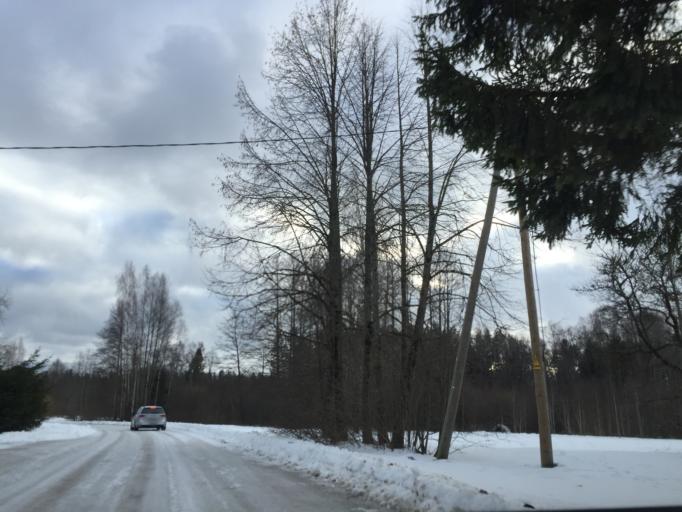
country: LV
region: Lielvarde
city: Lielvarde
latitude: 56.5780
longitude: 24.7896
